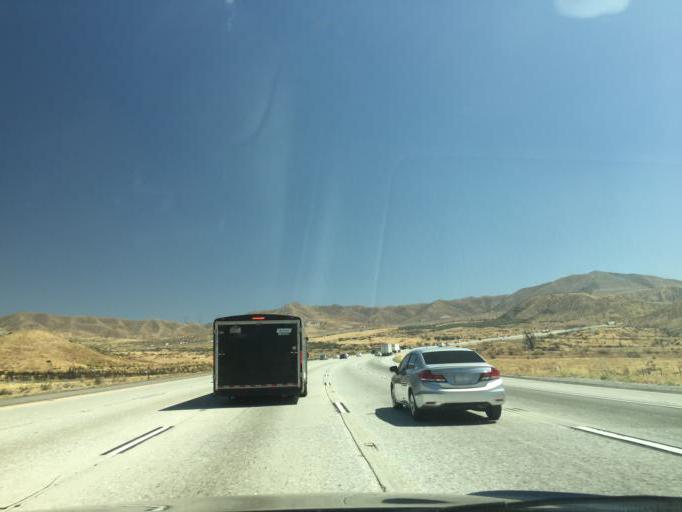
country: US
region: California
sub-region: San Bernardino County
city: Oak Hills
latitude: 34.3359
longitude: -117.4810
